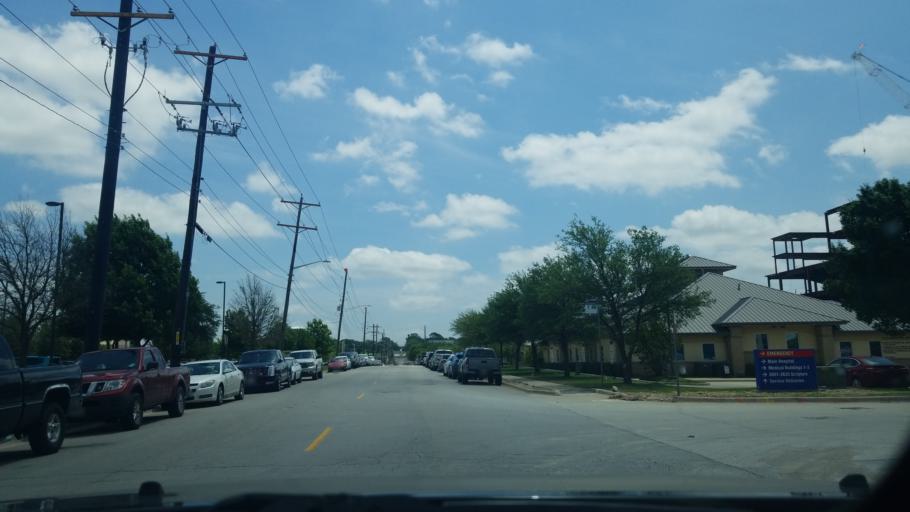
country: US
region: Texas
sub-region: Denton County
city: Denton
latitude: 33.2192
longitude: -97.1688
